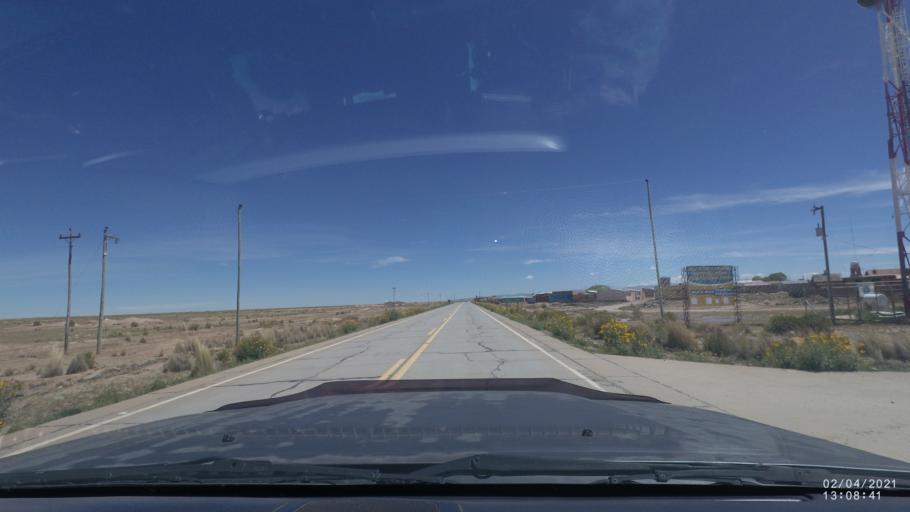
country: BO
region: Oruro
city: Oruro
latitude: -18.0785
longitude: -67.2364
